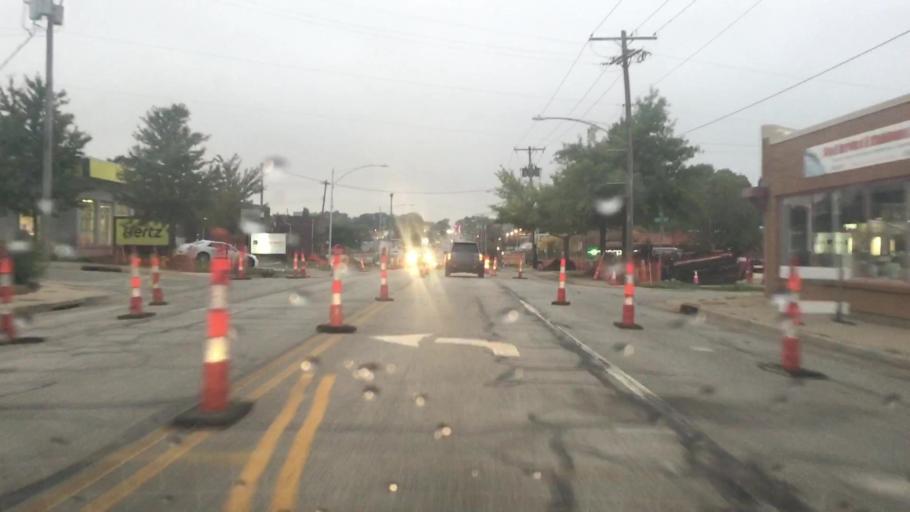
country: US
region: Kansas
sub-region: Johnson County
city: Merriam
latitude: 39.0206
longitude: -94.7146
